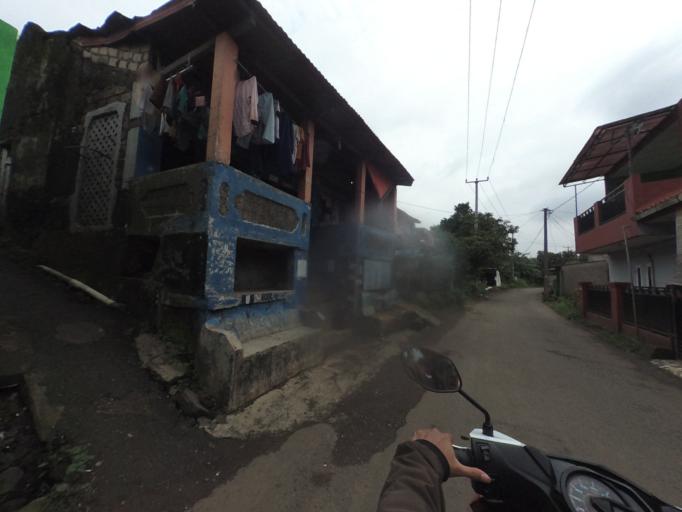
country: ID
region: West Java
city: Bogor
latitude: -6.6115
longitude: 106.7524
